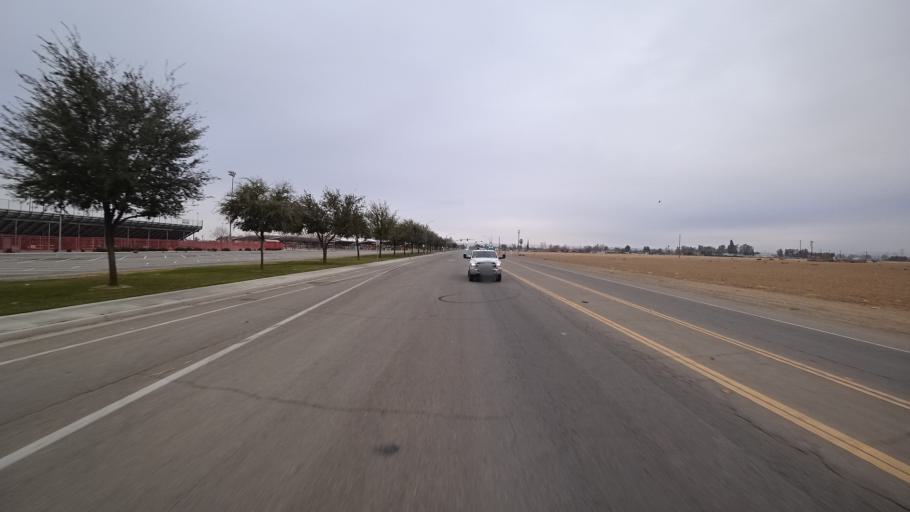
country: US
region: California
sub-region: Kern County
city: Lamont
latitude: 35.3345
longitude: -118.9321
